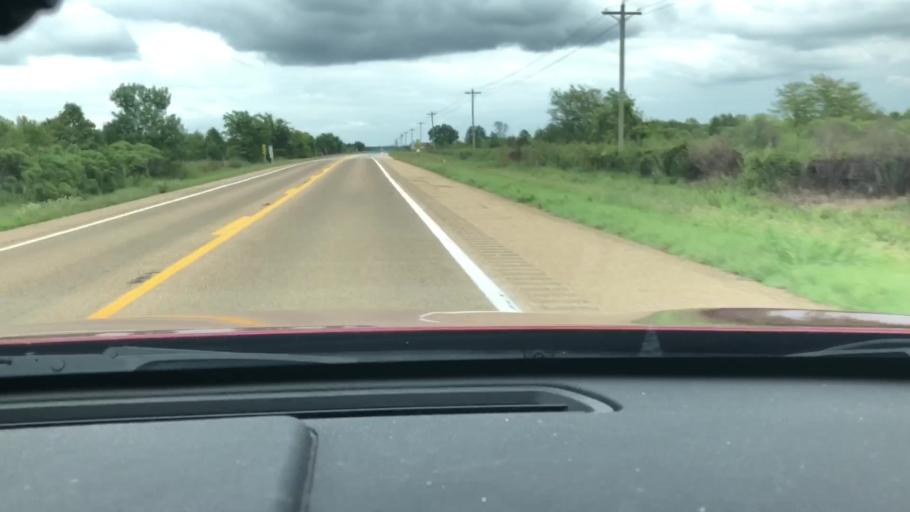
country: US
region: Arkansas
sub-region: Lafayette County
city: Lewisville
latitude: 33.4127
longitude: -93.8010
